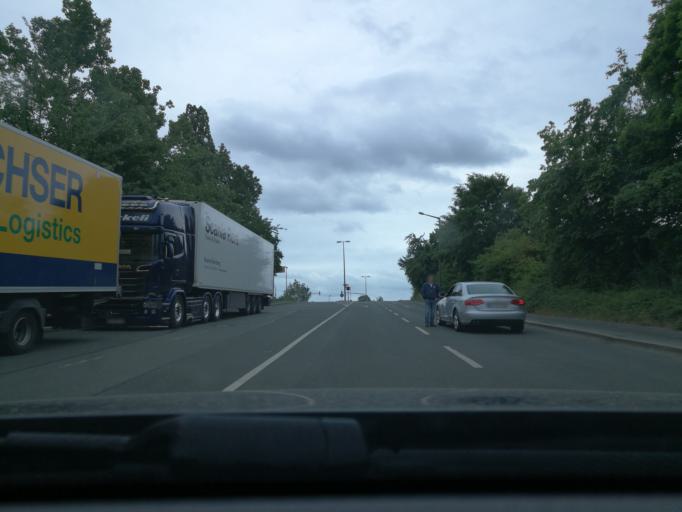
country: DE
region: Bavaria
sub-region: Regierungsbezirk Mittelfranken
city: Furth
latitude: 49.4866
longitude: 10.9486
